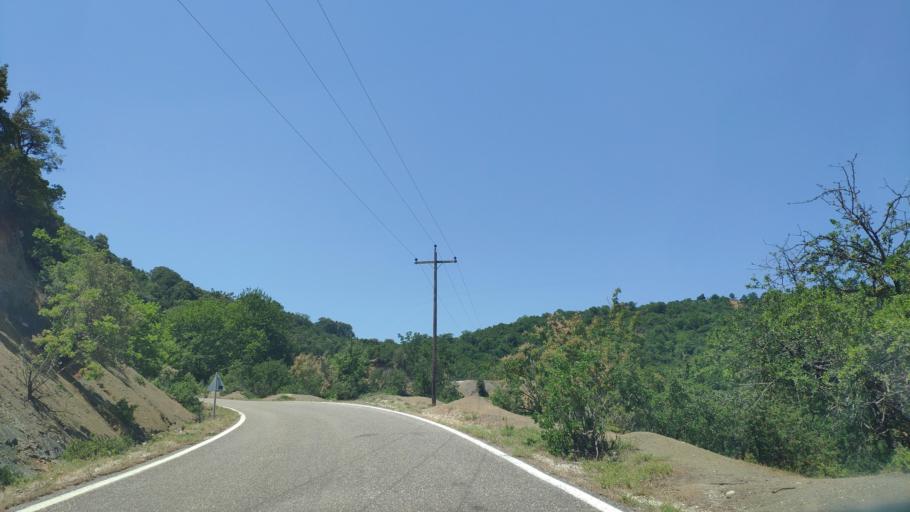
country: GR
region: West Greece
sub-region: Nomos Aitolias kai Akarnanias
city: Sardinia
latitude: 38.8562
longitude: 21.3111
